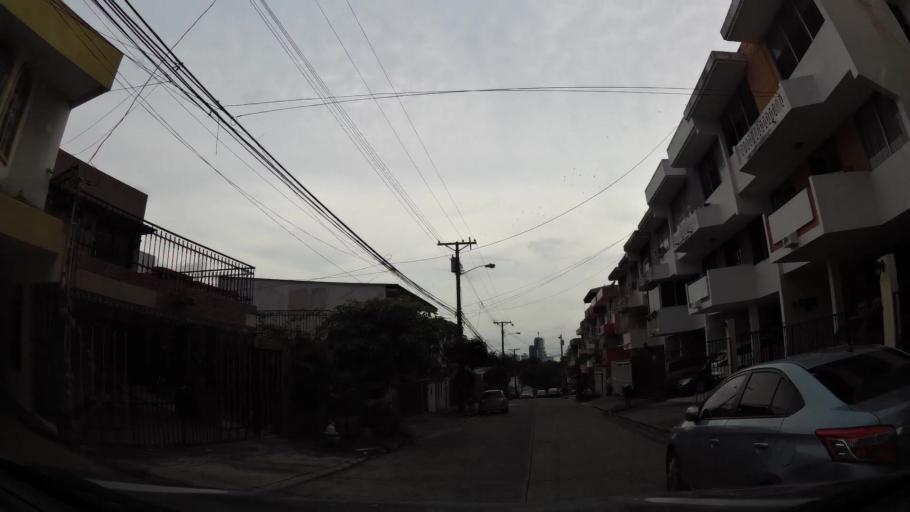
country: PA
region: Panama
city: Panama
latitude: 9.0138
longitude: -79.5327
